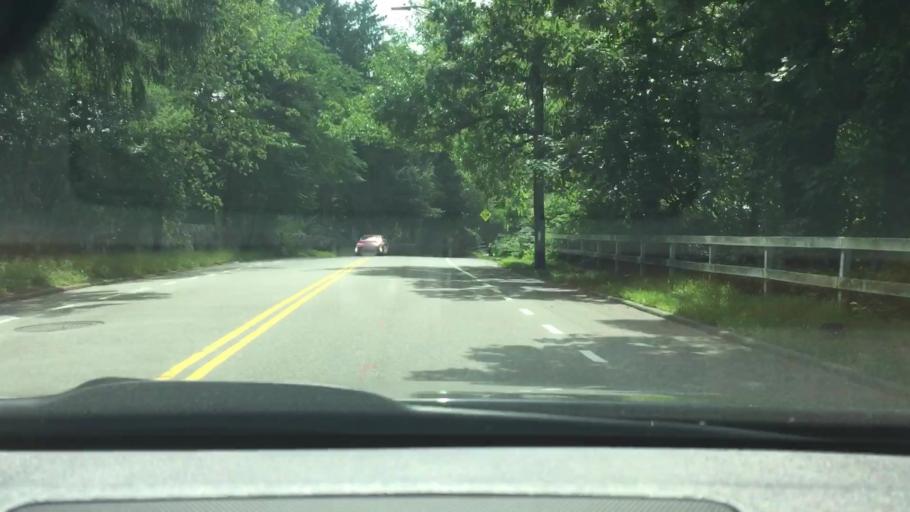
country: US
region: Massachusetts
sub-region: Norfolk County
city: Dedham
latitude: 42.2920
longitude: -71.1749
